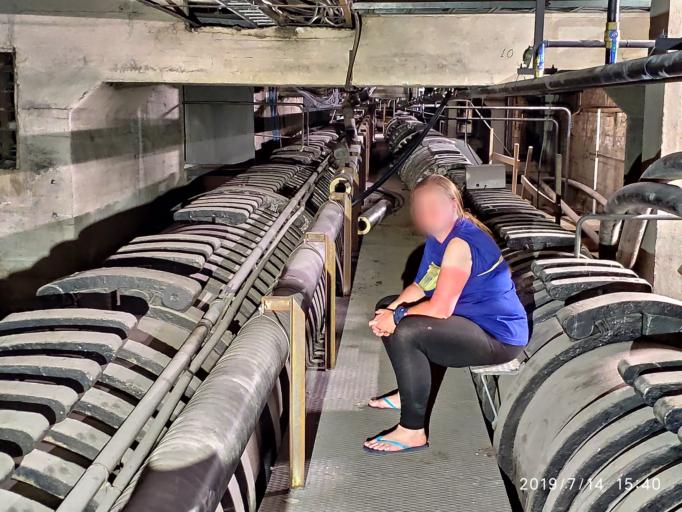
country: NO
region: Hordaland
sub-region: Odda
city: Odda
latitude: 60.1220
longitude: 6.5559
